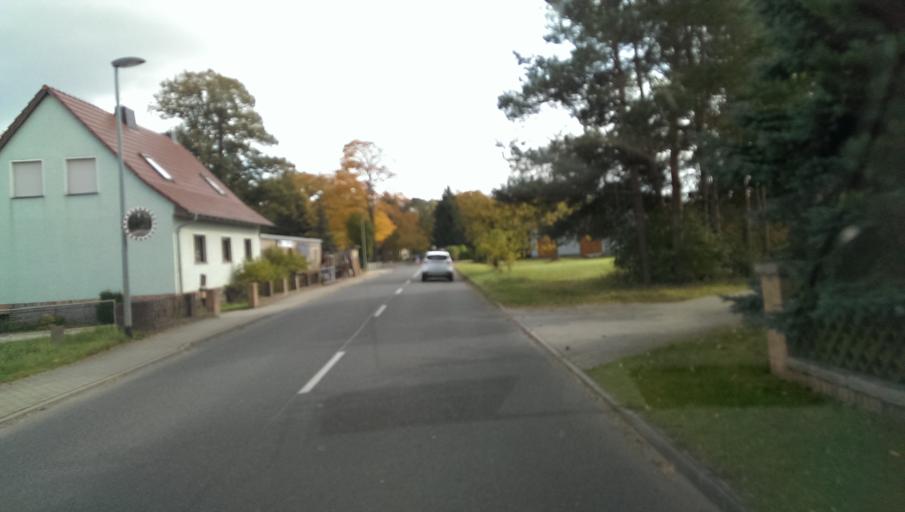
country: DE
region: Saxony
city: Wiednitz
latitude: 51.3878
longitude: 14.0288
